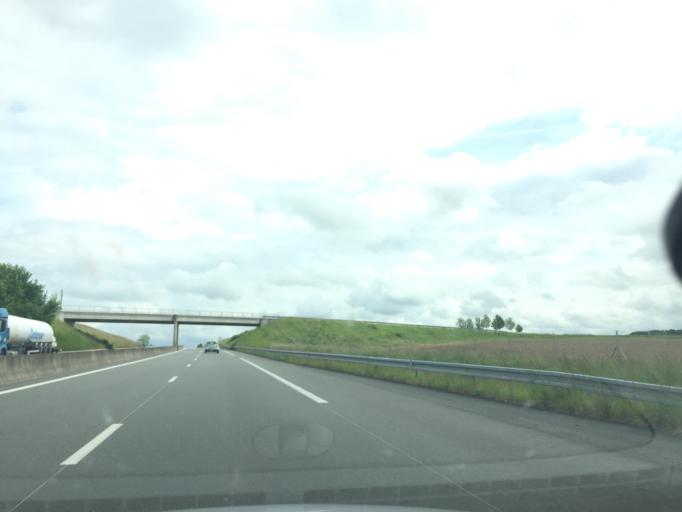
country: FR
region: Pays de la Loire
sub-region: Departement de la Sarthe
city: Chateau-du-Loir
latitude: 47.6565
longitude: 0.4401
